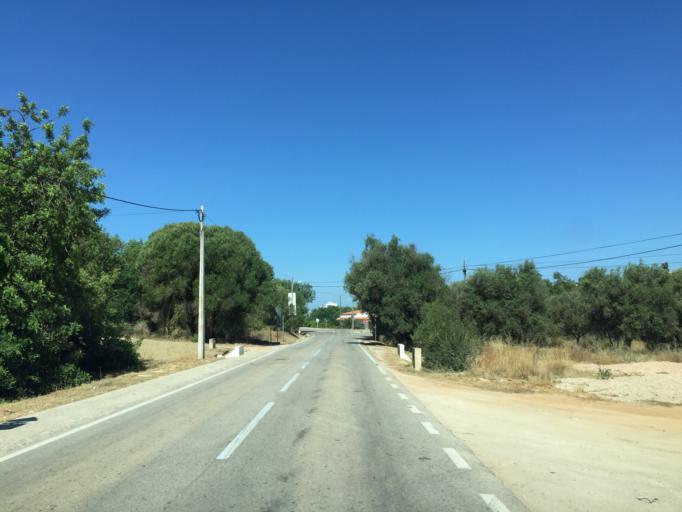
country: PT
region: Faro
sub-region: Loule
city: Vilamoura
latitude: 37.1190
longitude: -8.0962
